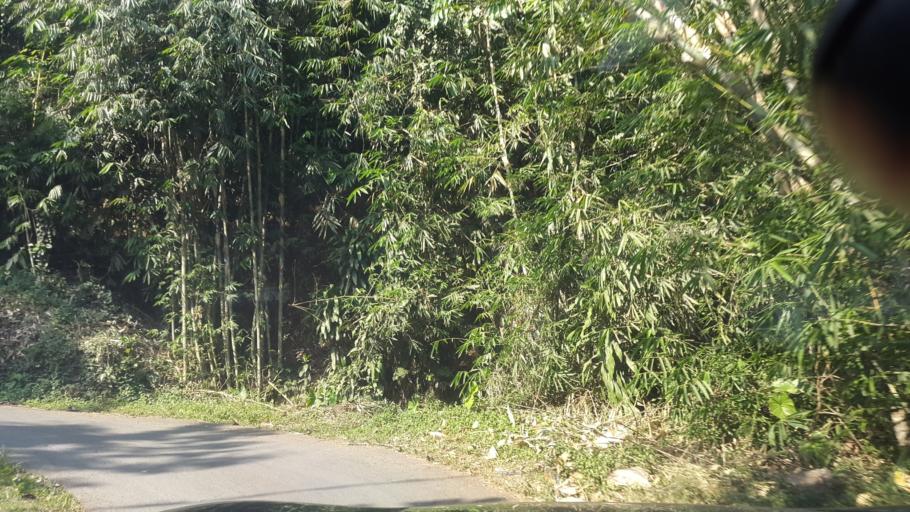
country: ID
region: West Java
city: Cicurug
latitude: -6.8786
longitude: 106.8210
